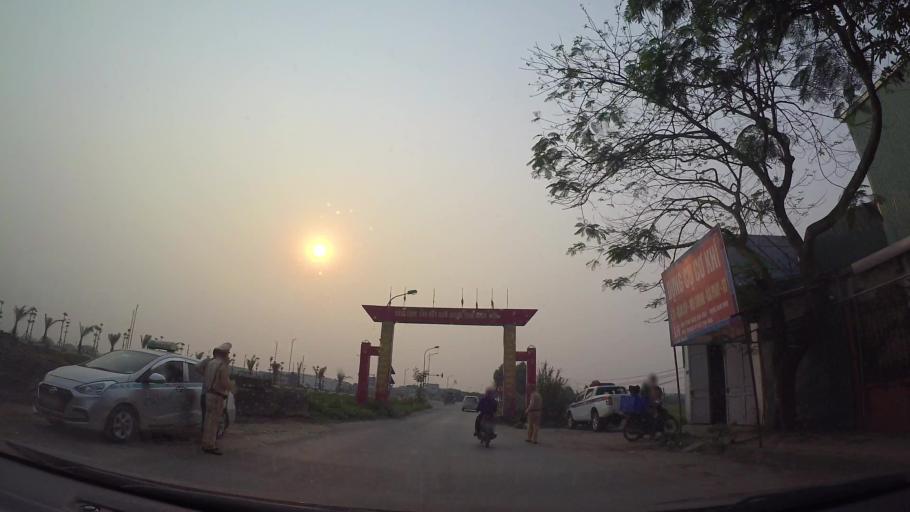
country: VN
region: Ha Noi
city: Kim Bai
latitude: 20.8719
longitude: 105.8044
